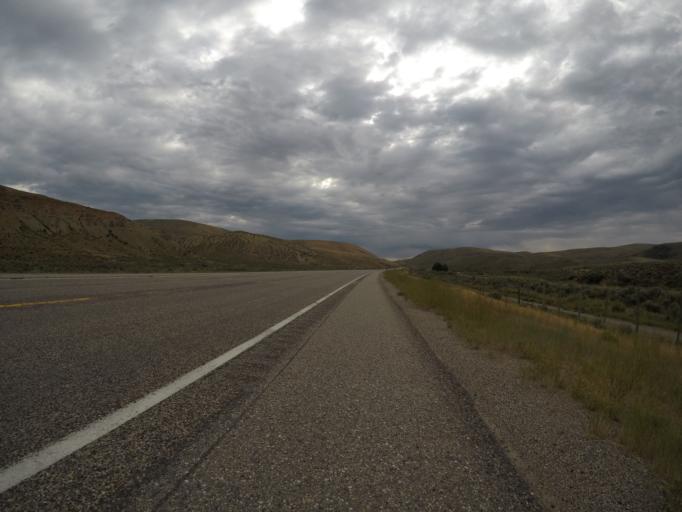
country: US
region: Wyoming
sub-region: Lincoln County
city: Kemmerer
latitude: 41.8229
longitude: -110.8782
